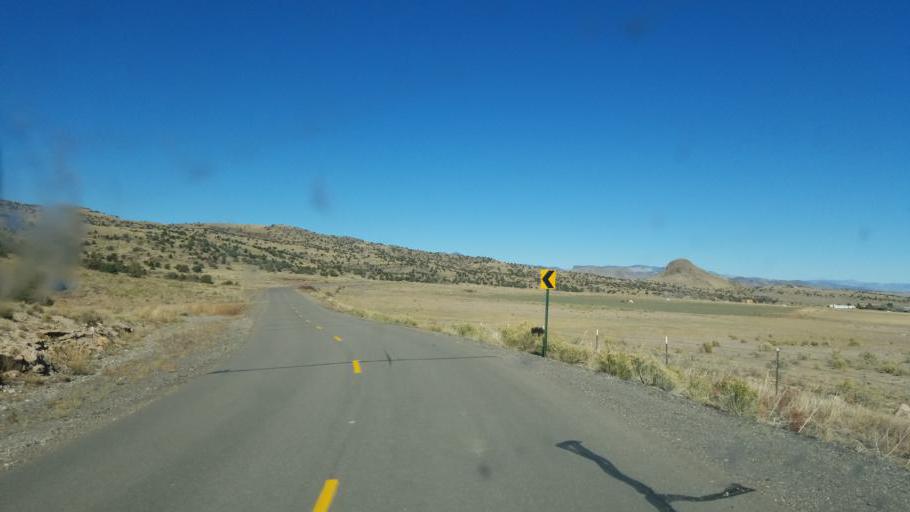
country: US
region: Colorado
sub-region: Rio Grande County
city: Del Norte
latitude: 37.6440
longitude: -106.3633
